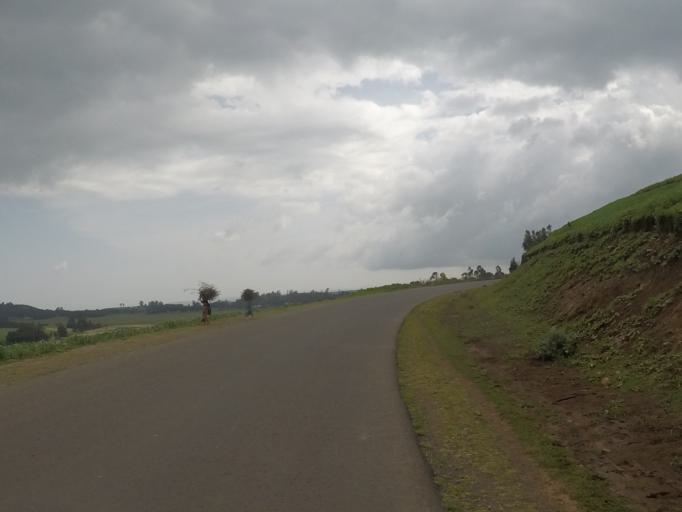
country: ET
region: Amhara
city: Dabat
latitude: 13.0546
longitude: 37.8208
